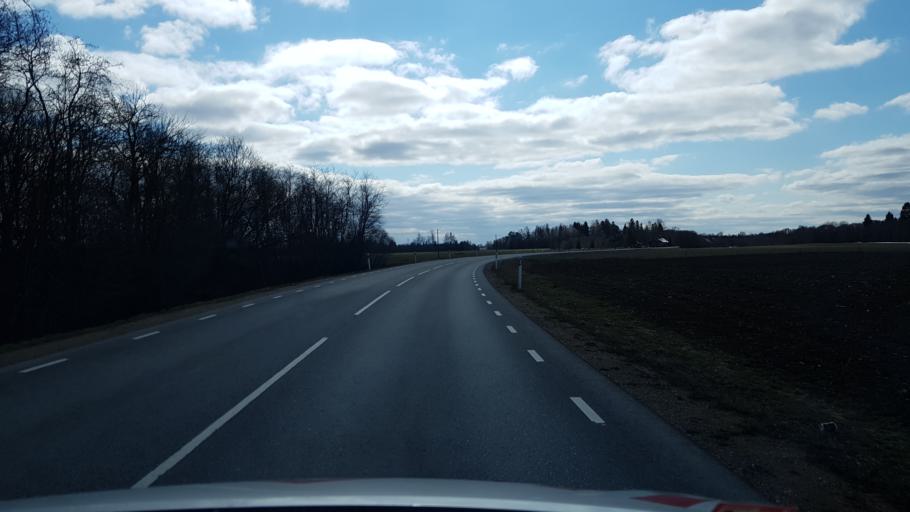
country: EE
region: Laeaene-Virumaa
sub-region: Tapa vald
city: Tapa
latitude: 59.3464
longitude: 26.0058
